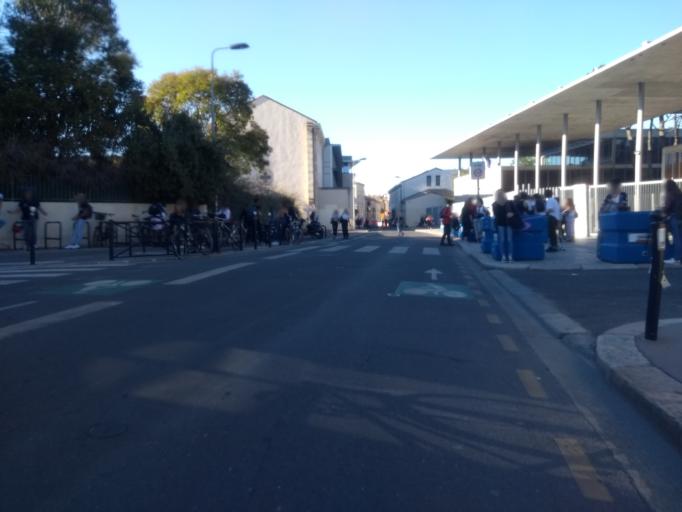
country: FR
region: Aquitaine
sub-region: Departement de la Gironde
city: Bordeaux
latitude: 44.8265
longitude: -0.5852
